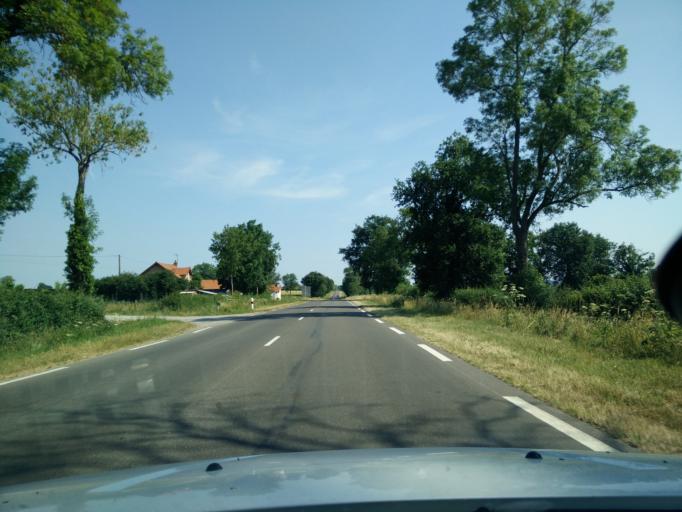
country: FR
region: Auvergne
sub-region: Departement de l'Allier
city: Toulon-sur-Allier
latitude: 46.4970
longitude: 3.3160
